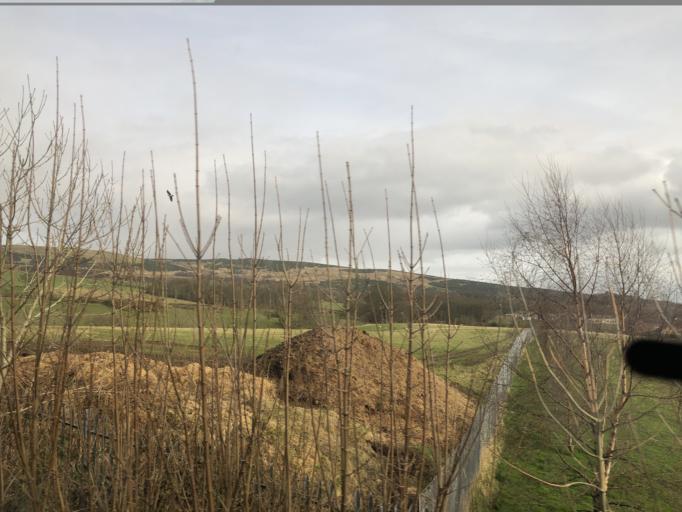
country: GB
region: Scotland
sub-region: Argyll and Bute
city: Helensburgh
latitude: 56.0018
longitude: -4.7101
